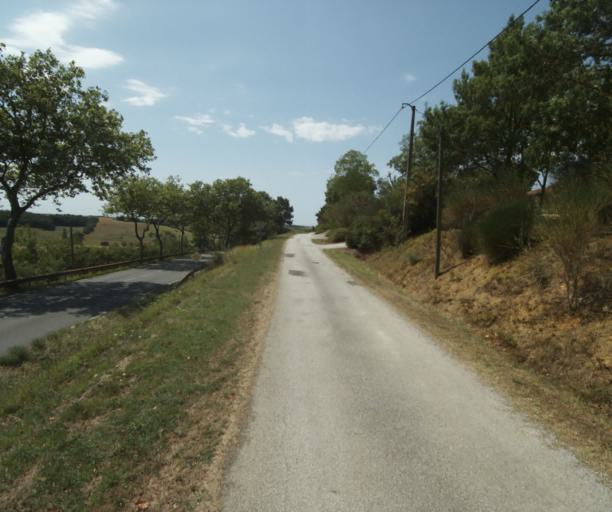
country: FR
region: Midi-Pyrenees
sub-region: Departement de la Haute-Garonne
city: Saint-Felix-Lauragais
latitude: 43.4550
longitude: 1.8699
